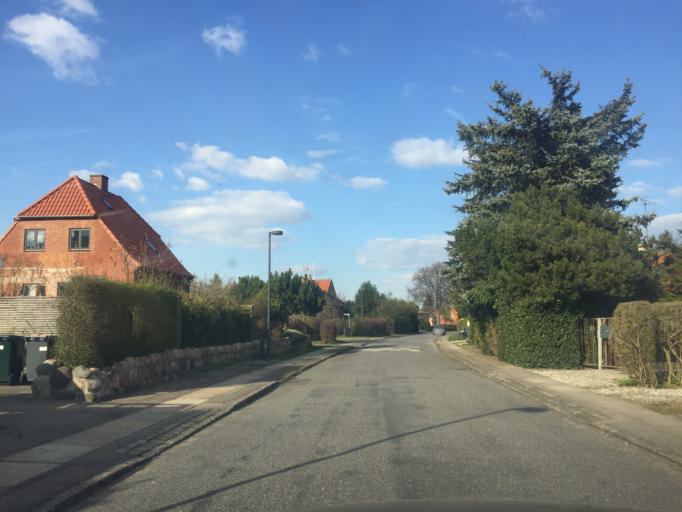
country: DK
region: Capital Region
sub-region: Herlev Kommune
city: Herlev
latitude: 55.7065
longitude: 12.4602
